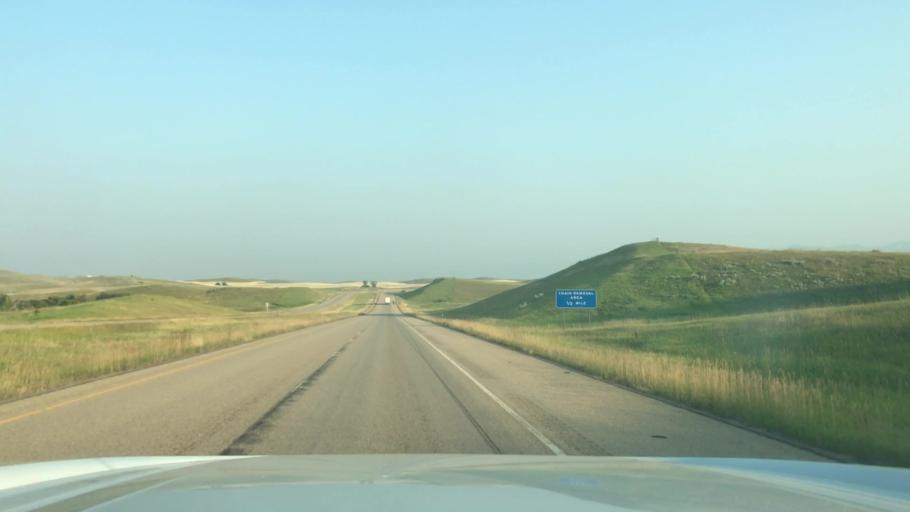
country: US
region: Wyoming
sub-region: Sheridan County
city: Sheridan
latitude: 45.0154
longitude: -107.3064
